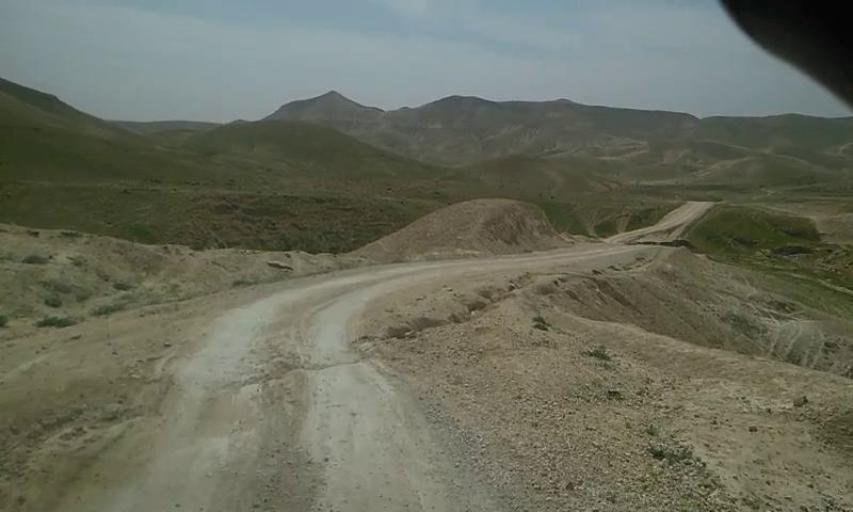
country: PS
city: `Arab ar Rashaydah
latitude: 31.5144
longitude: 35.2849
